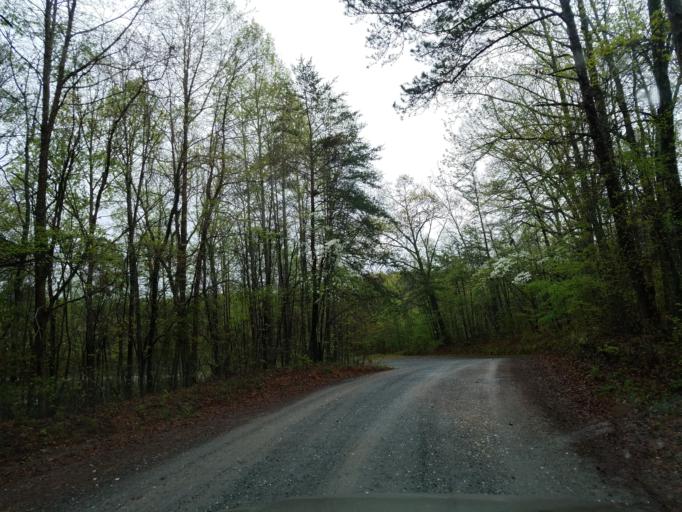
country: US
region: Georgia
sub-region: Pickens County
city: Jasper
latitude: 34.5467
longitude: -84.5268
